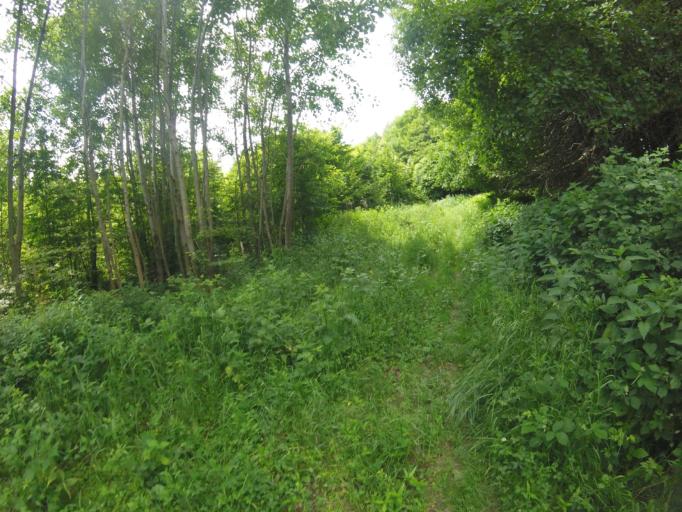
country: HU
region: Veszprem
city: Urkut
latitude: 47.0941
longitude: 17.6480
